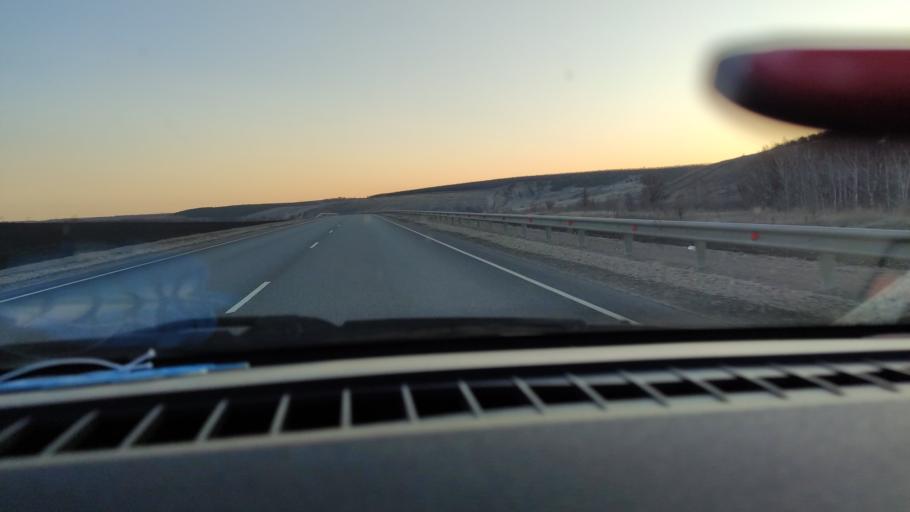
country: RU
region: Saratov
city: Yelshanka
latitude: 51.8606
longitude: 46.4983
